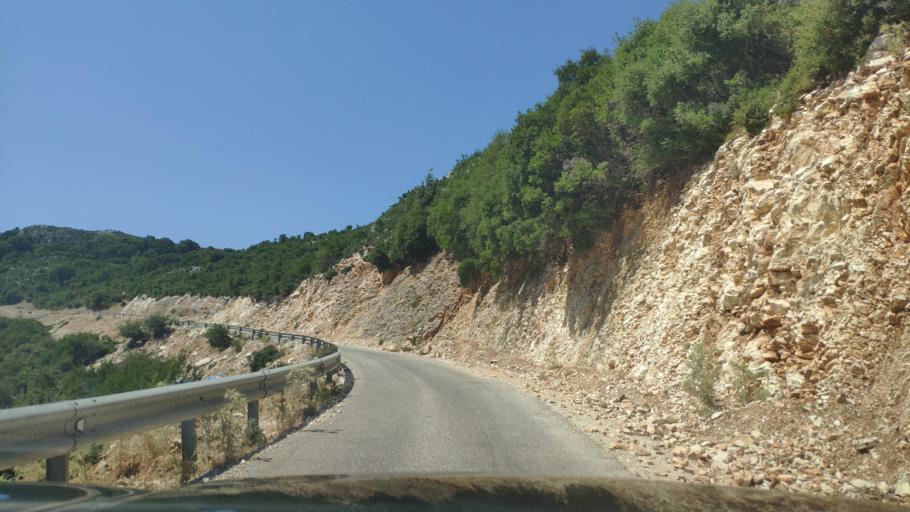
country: GR
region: West Greece
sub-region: Nomos Aitolias kai Akarnanias
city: Monastirakion
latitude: 38.8293
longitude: 20.9289
